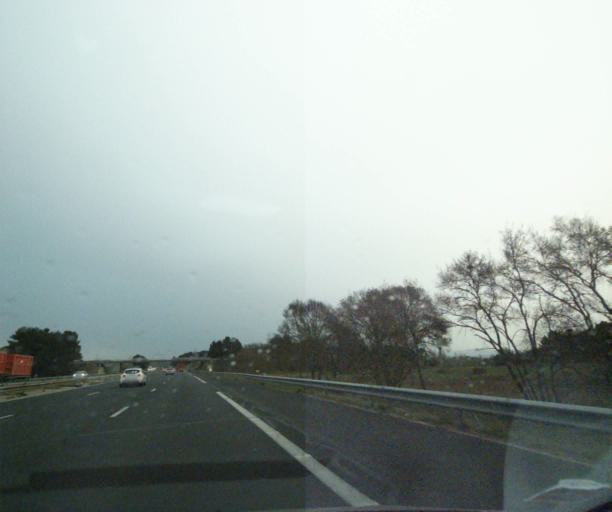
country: FR
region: Provence-Alpes-Cote d'Azur
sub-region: Departement des Bouches-du-Rhone
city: Eguilles
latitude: 43.5375
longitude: 5.3461
